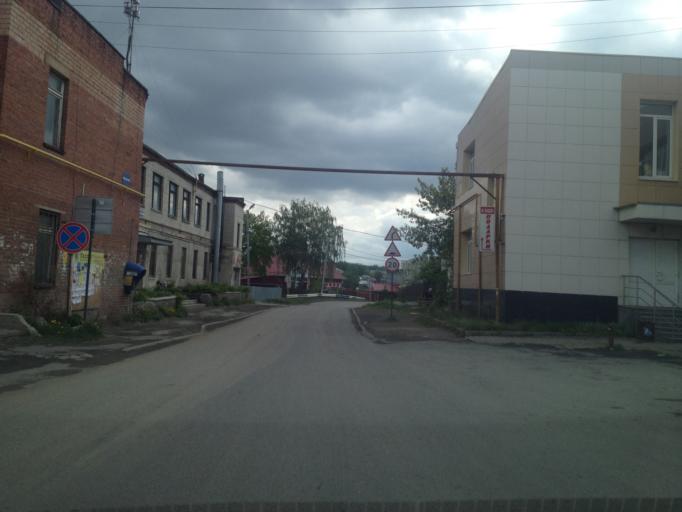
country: RU
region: Sverdlovsk
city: Aramil
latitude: 56.6985
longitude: 60.8323
